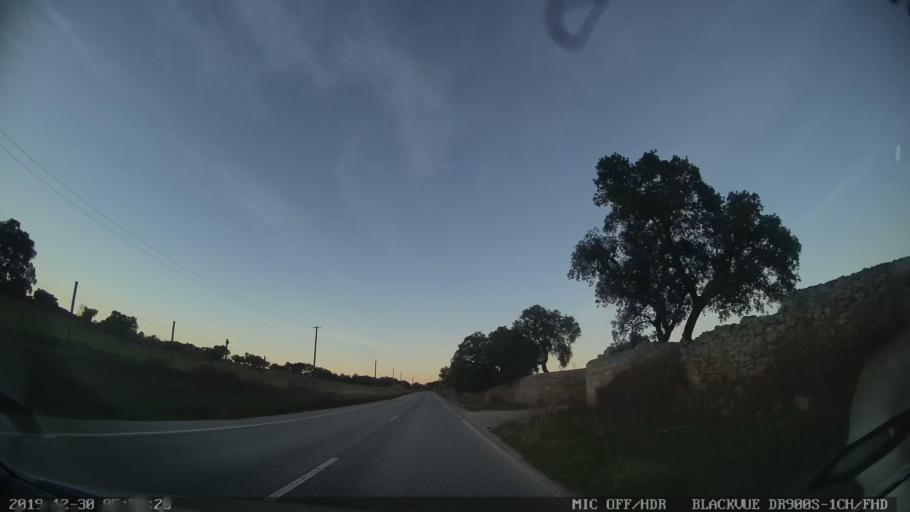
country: PT
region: Castelo Branco
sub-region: Idanha-A-Nova
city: Idanha-a-Nova
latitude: 40.0337
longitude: -7.2415
